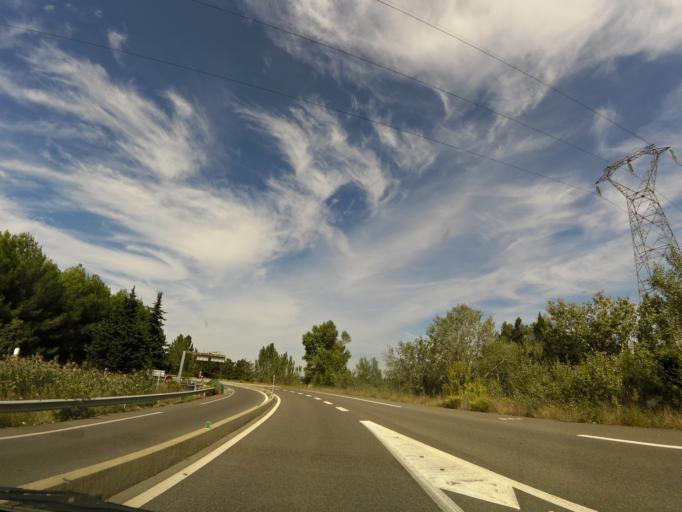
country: FR
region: Languedoc-Roussillon
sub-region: Departement du Gard
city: Caissargues
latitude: 43.8057
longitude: 4.3768
